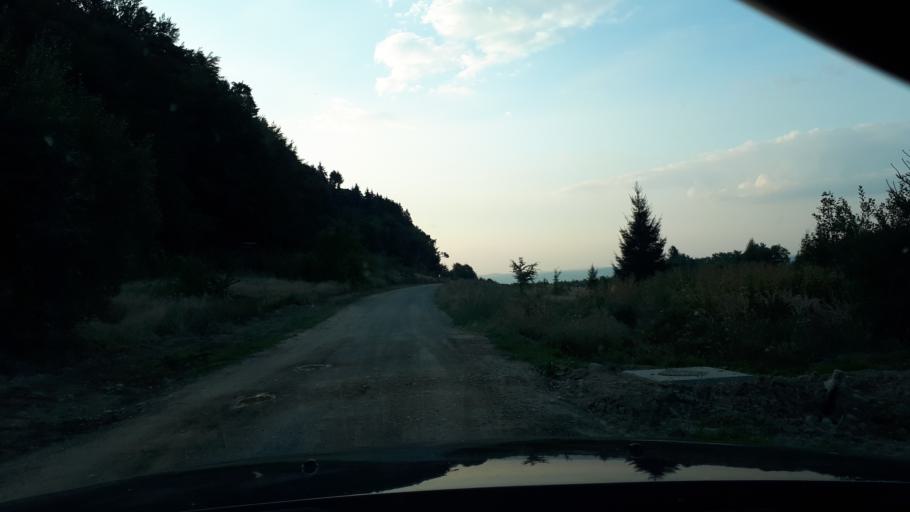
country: RO
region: Brasov
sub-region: Comuna Lisa
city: Lisa
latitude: 45.6888
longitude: 24.7915
